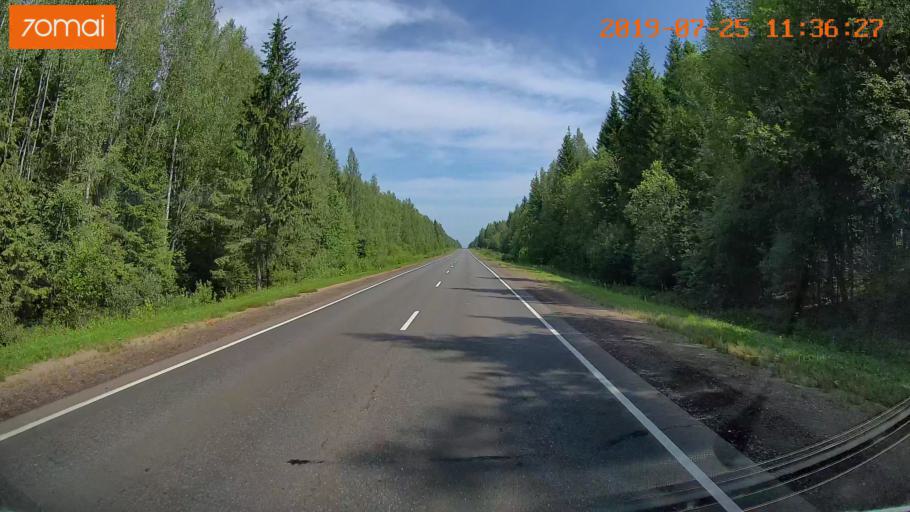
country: RU
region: Ivanovo
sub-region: Privolzhskiy Rayon
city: Ples
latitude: 57.4229
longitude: 41.4488
